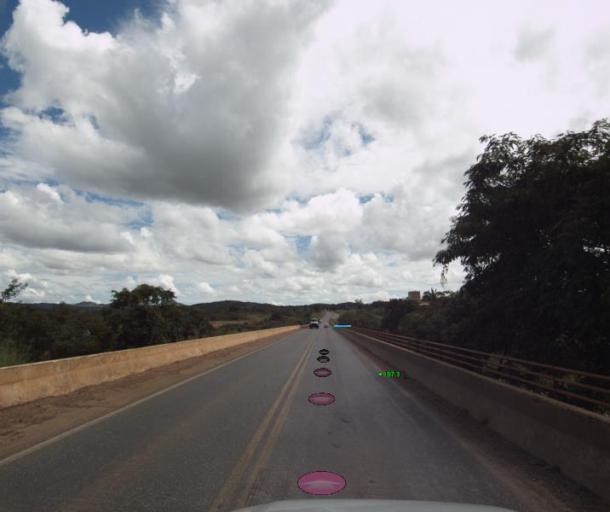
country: BR
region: Goias
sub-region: Uruacu
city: Uruacu
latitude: -14.5045
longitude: -49.1490
